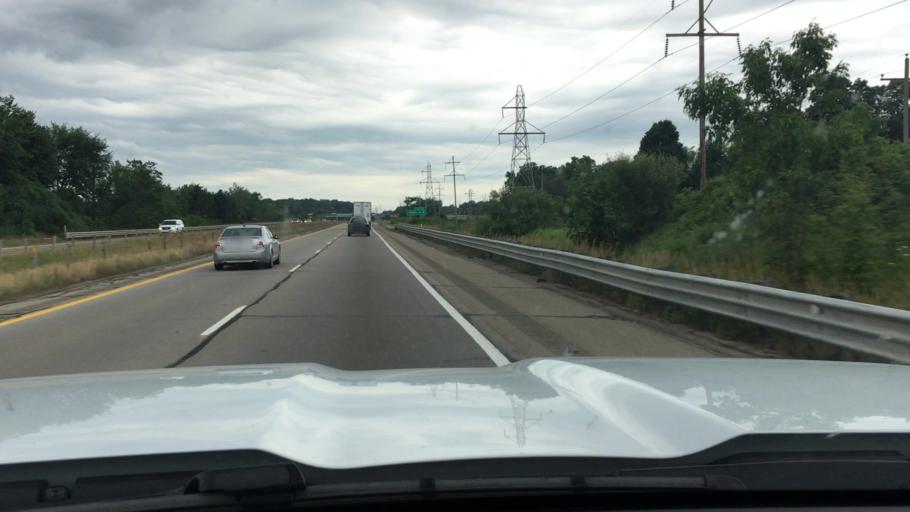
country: US
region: Michigan
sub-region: Kent County
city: Cutlerville
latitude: 42.7888
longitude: -85.6685
